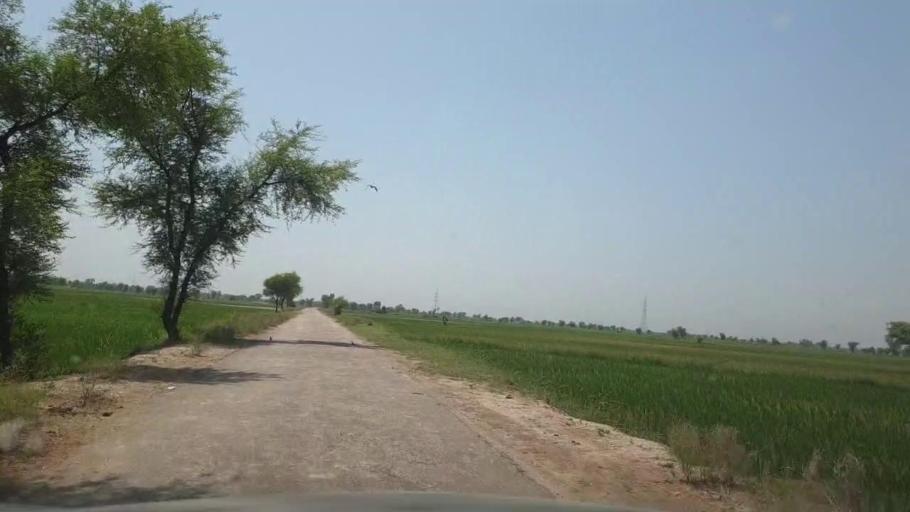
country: PK
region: Sindh
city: Warah
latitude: 27.5010
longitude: 67.7564
